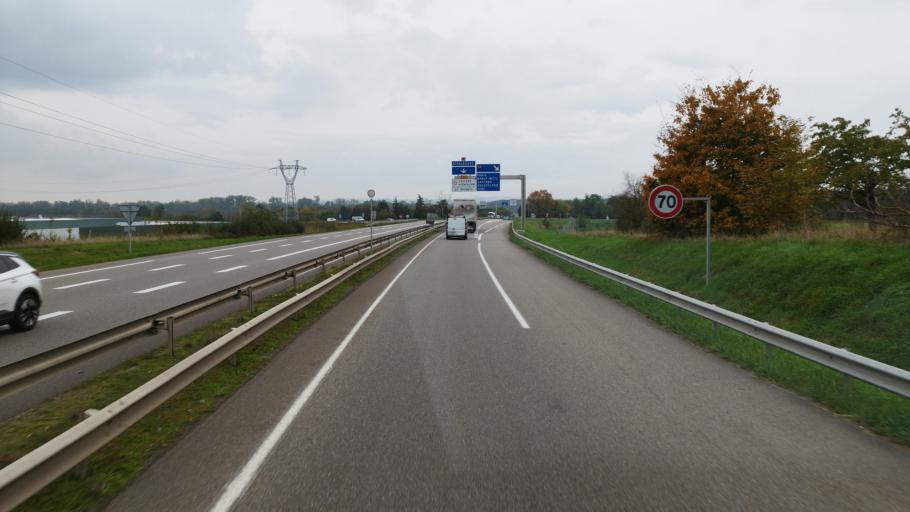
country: FR
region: Alsace
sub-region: Departement du Bas-Rhin
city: Brumath
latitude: 48.7502
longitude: 7.6877
